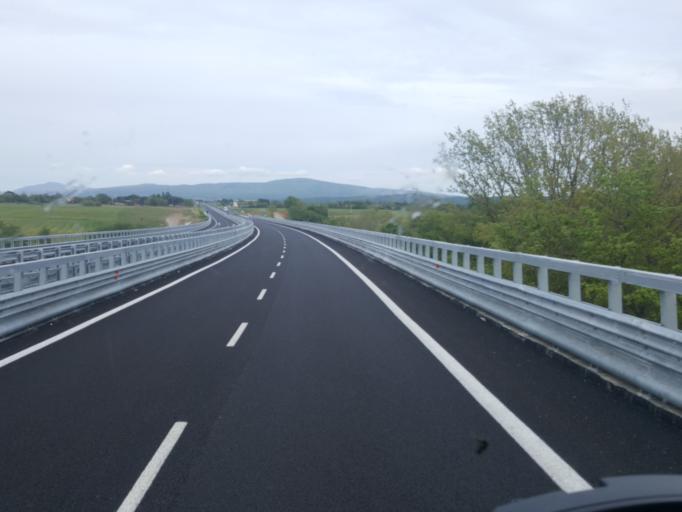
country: IT
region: Latium
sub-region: Provincia di Viterbo
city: Blera
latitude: 42.2972
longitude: 11.9626
